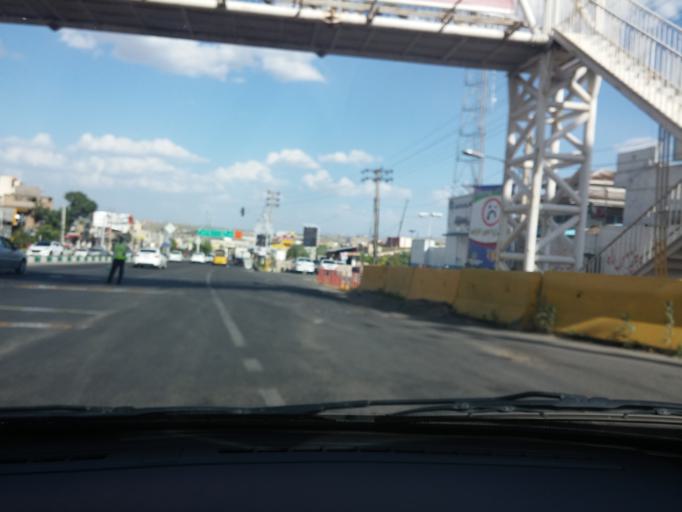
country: IR
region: Tehran
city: Damavand
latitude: 35.6878
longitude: 52.0130
